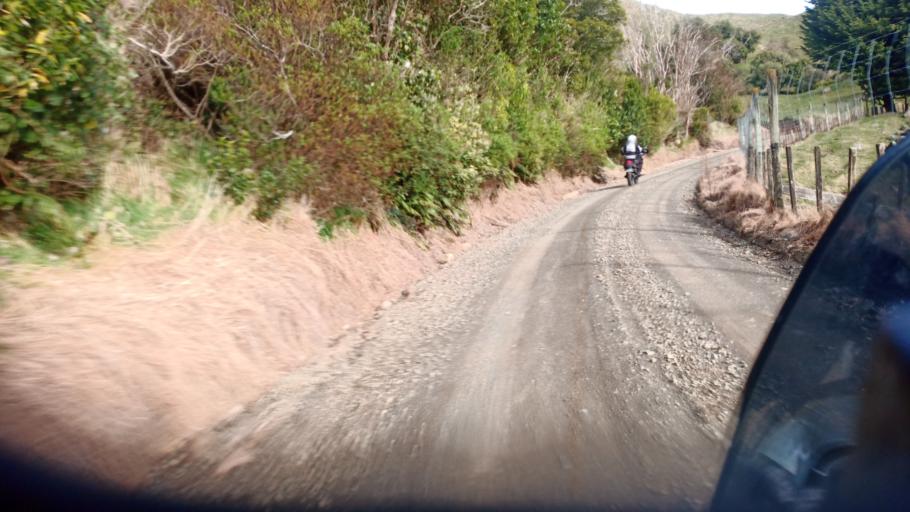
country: NZ
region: Gisborne
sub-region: Gisborne District
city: Gisborne
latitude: -38.4612
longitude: 177.5388
